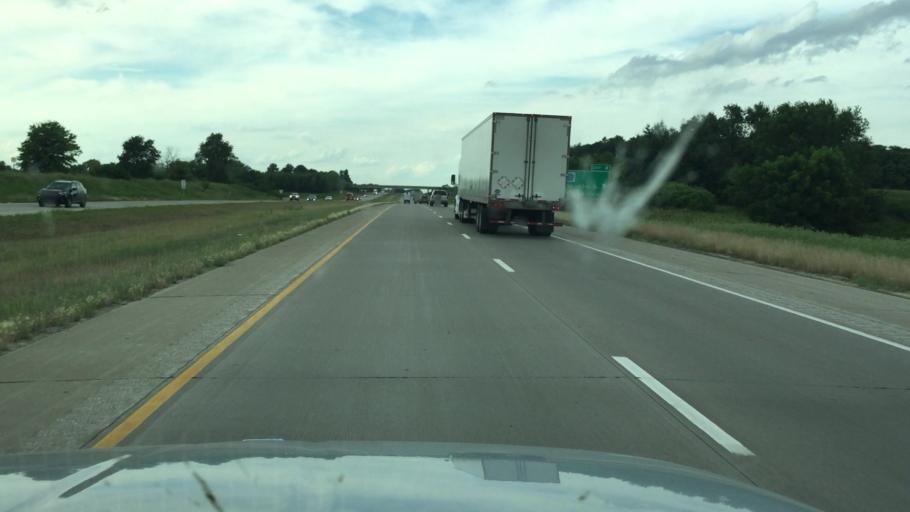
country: US
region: Iowa
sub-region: Scott County
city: Buffalo
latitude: 41.5316
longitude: -90.6750
